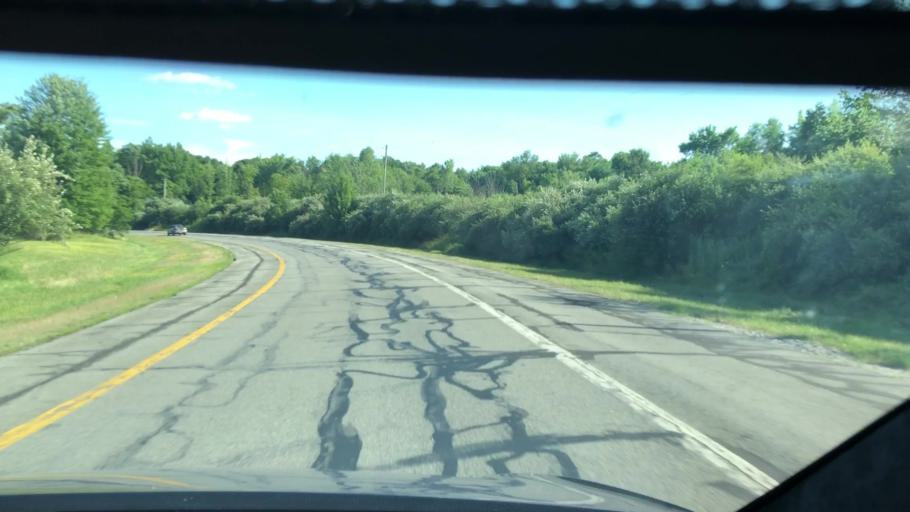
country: US
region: Ohio
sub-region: Mahoning County
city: Boardman
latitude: 40.9544
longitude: -80.6402
